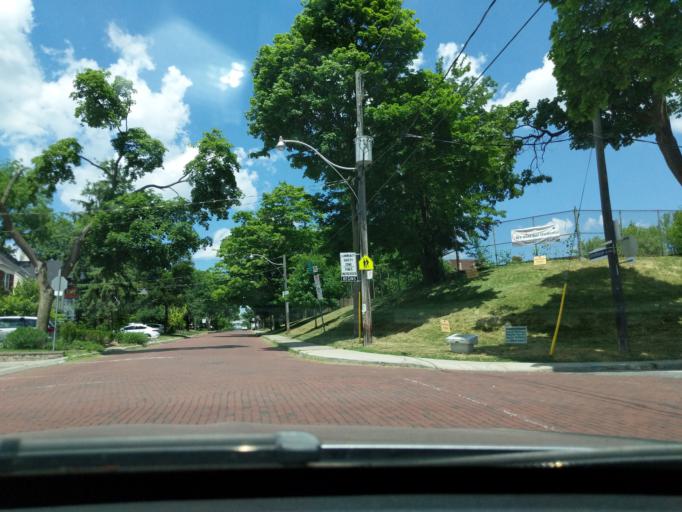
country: CA
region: Ontario
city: Toronto
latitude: 43.7013
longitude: -79.4098
